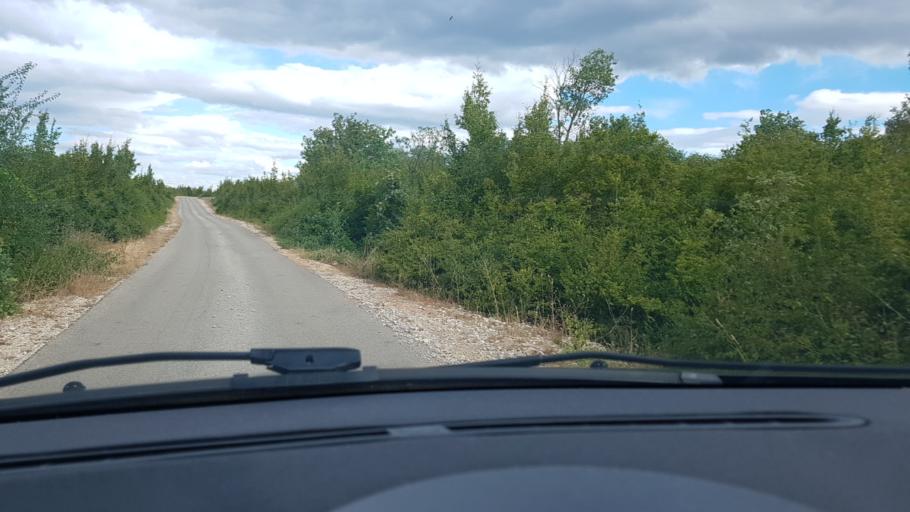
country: HR
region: Sibensko-Kniniska
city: Kistanje
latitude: 44.1137
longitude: 15.9148
